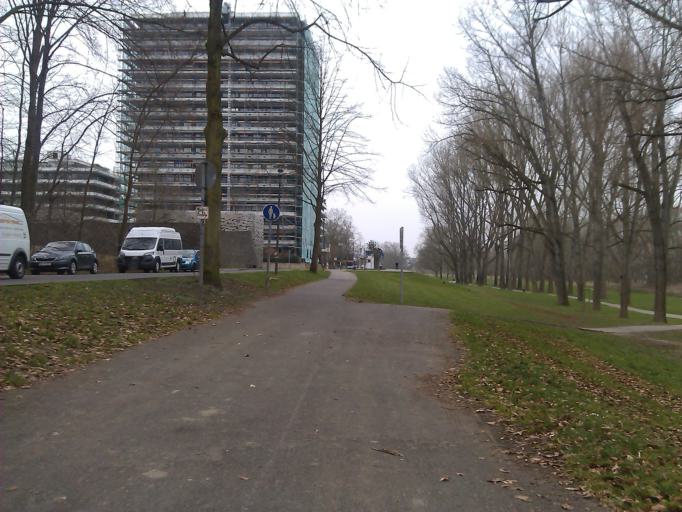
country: DE
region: North Rhine-Westphalia
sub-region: Regierungsbezirk Koln
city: Poll
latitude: 50.8916
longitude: 7.0125
